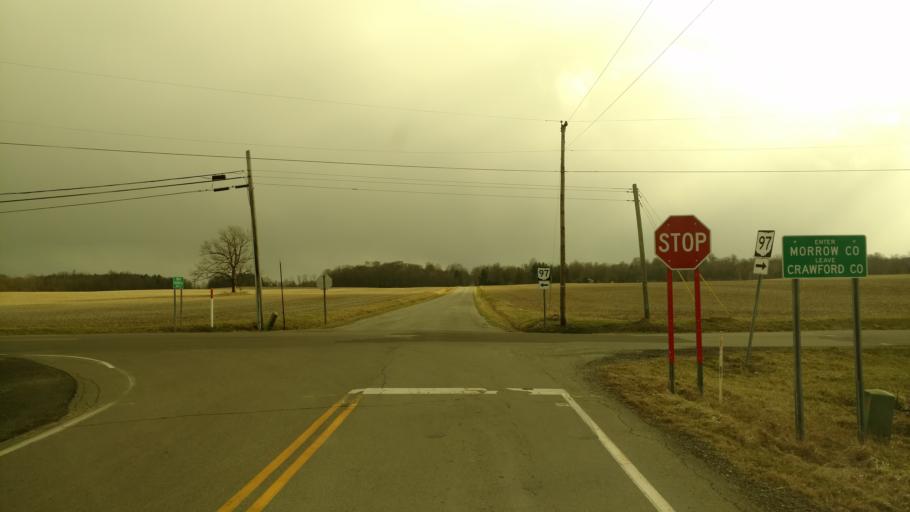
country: US
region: Ohio
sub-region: Crawford County
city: Galion
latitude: 40.7115
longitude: -82.7318
